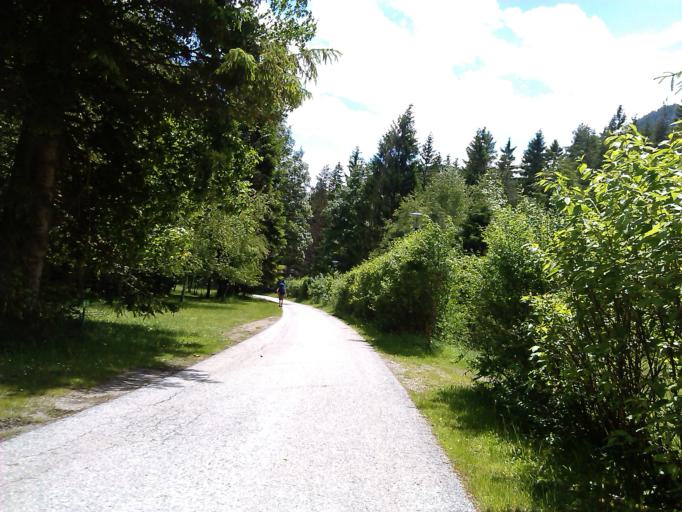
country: AT
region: Tyrol
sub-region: Politischer Bezirk Imst
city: Nassereith
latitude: 47.3415
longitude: 10.8150
